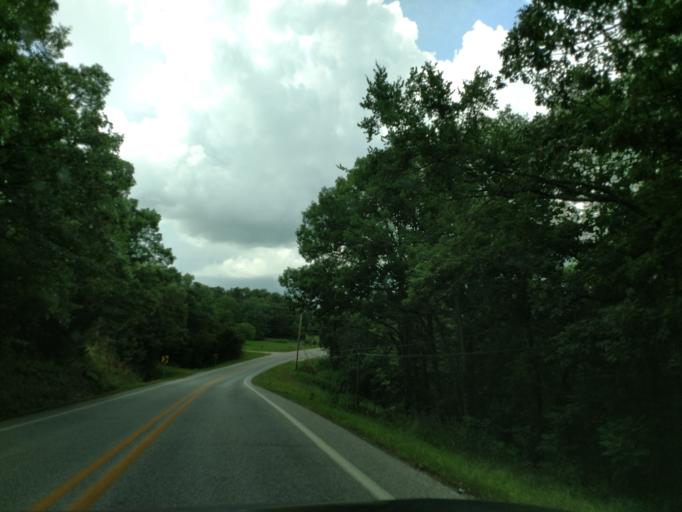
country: US
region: Arkansas
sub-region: Boone County
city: Harrison
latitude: 36.2420
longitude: -93.2119
